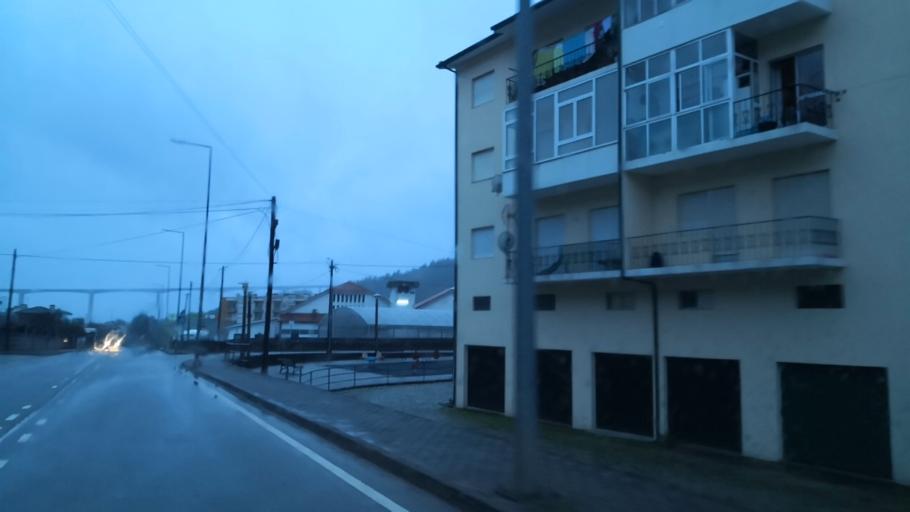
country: PT
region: Vila Real
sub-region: Vila Pouca de Aguiar
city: Vila Pouca de Aguiar
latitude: 41.4953
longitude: -7.6434
